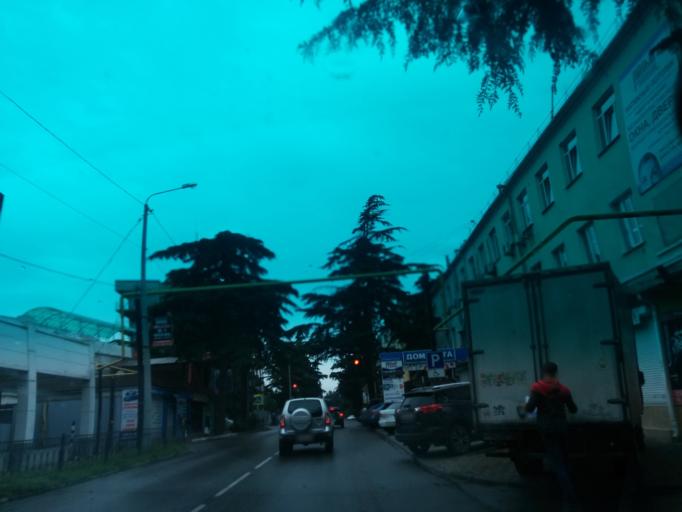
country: RU
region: Krasnodarskiy
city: Tuapse
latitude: 44.0955
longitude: 39.0769
